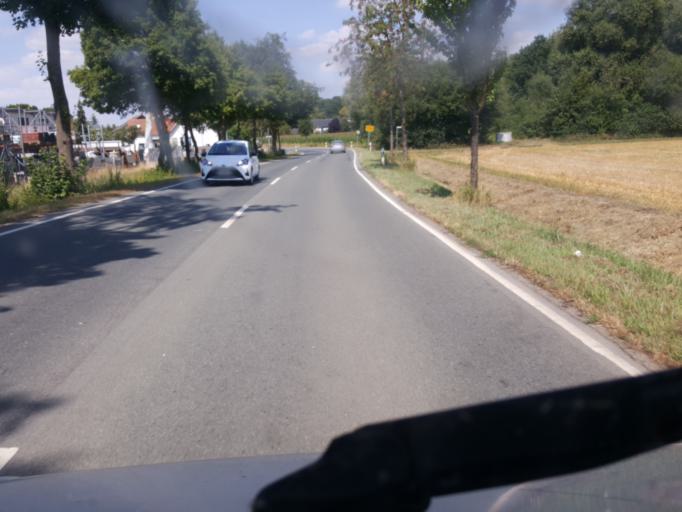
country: DE
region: North Rhine-Westphalia
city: Bad Oeynhausen
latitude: 52.2379
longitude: 8.7509
